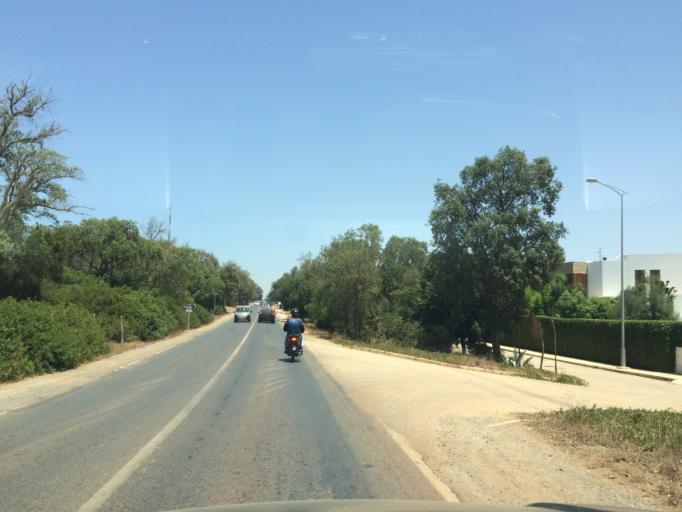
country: MA
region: Rabat-Sale-Zemmour-Zaer
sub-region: Skhirate-Temara
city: Temara
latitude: 33.9075
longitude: -6.8197
